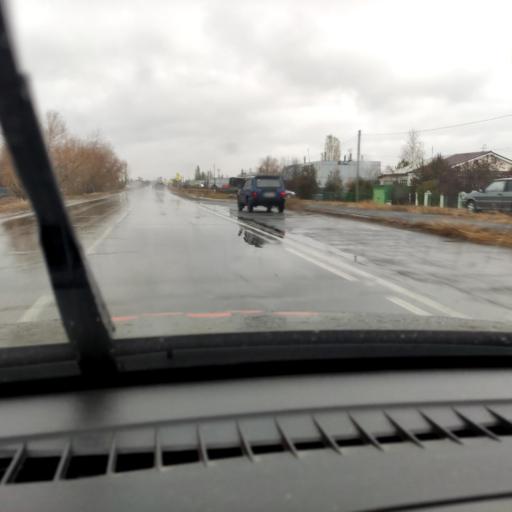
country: RU
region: Samara
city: Tol'yatti
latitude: 53.6384
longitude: 49.2981
